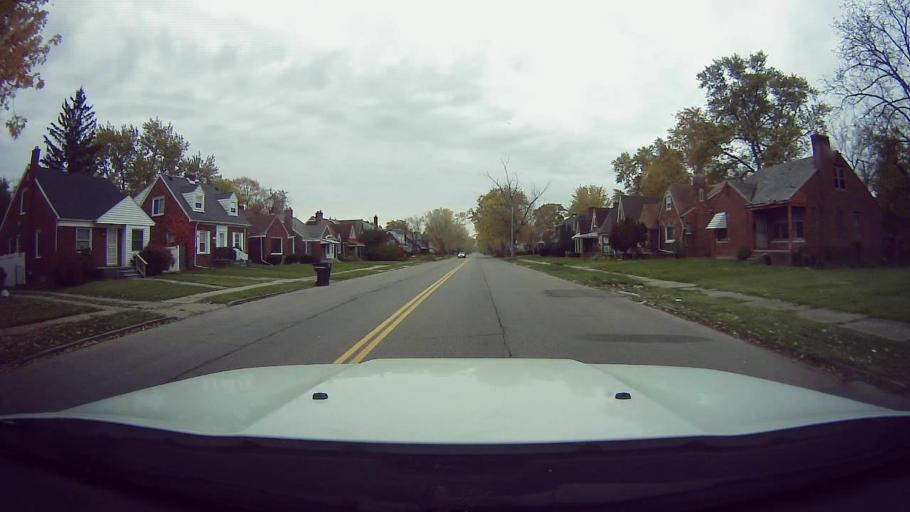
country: US
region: Michigan
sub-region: Oakland County
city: Oak Park
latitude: 42.3983
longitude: -83.1888
